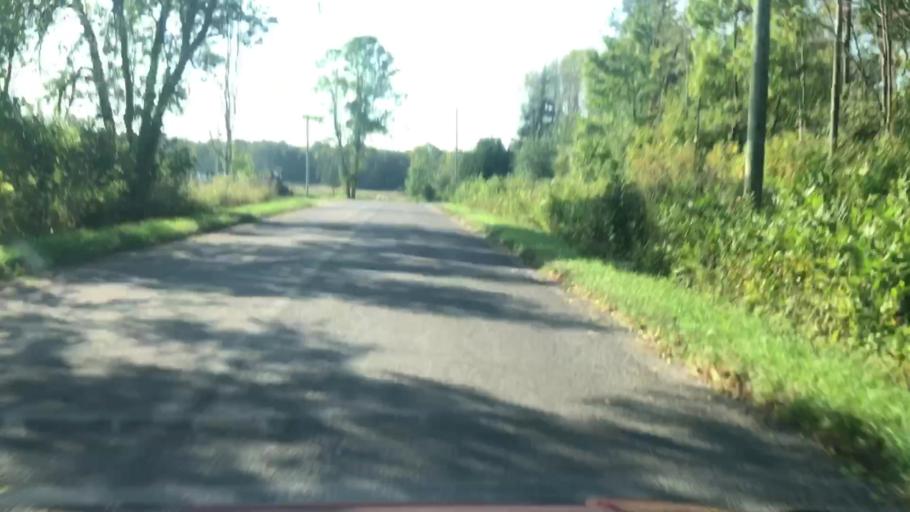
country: US
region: Michigan
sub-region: Chippewa County
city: Sault Ste. Marie
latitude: 46.2933
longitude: -84.0694
